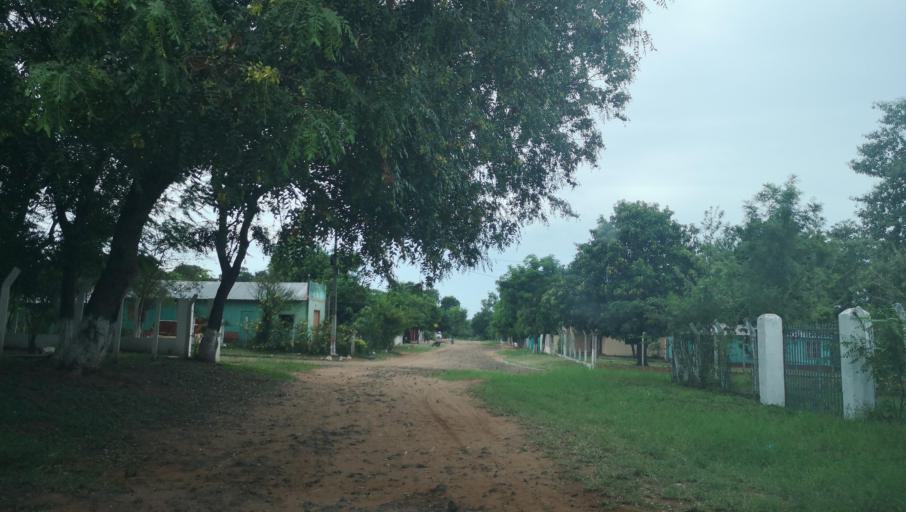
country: PY
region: San Pedro
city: Capiibary
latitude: -24.7266
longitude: -56.0132
